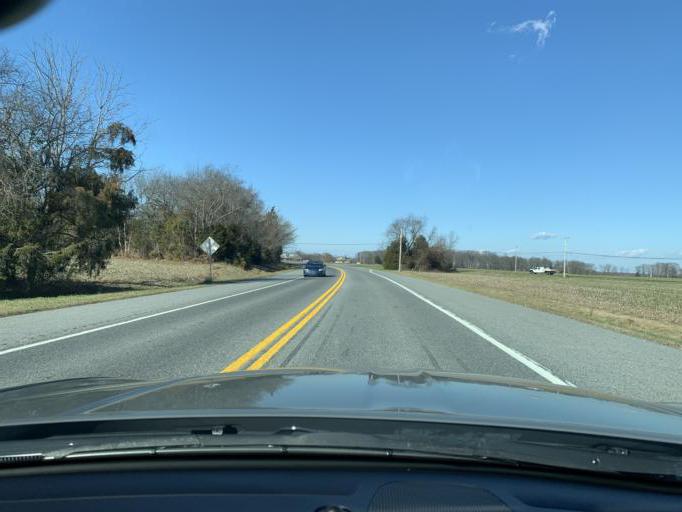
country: US
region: Maryland
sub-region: Queen Anne's County
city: Kingstown
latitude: 39.1679
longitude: -75.9860
